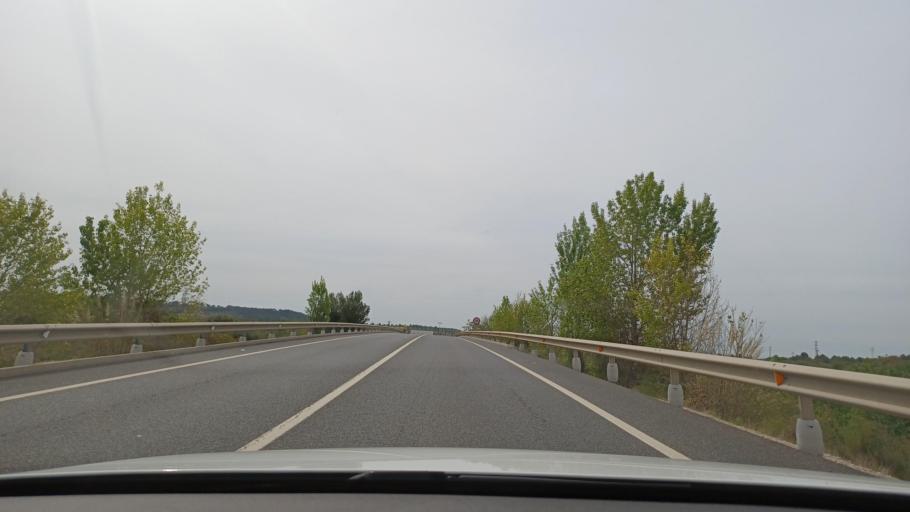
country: ES
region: Catalonia
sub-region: Provincia de Tarragona
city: la Pobla de Mafumet
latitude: 41.1964
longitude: 1.2427
